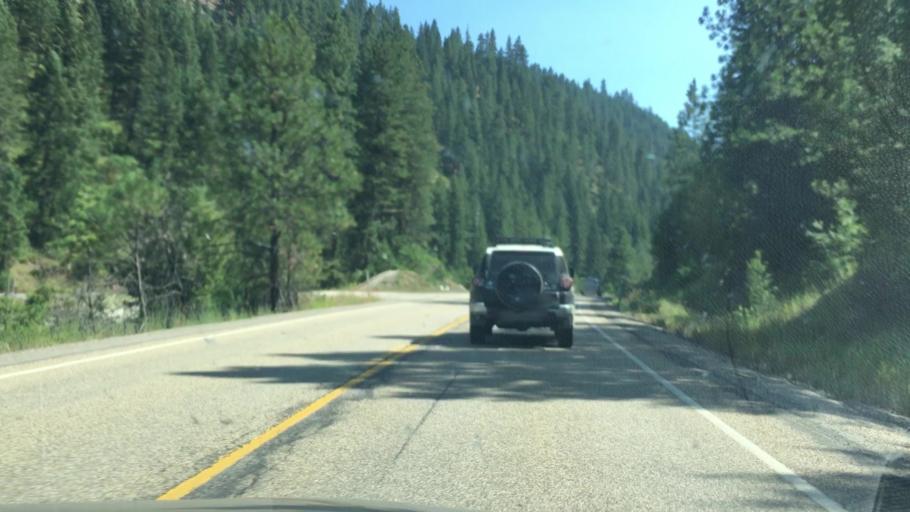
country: US
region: Idaho
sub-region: Valley County
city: Cascade
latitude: 44.2126
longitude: -116.1071
